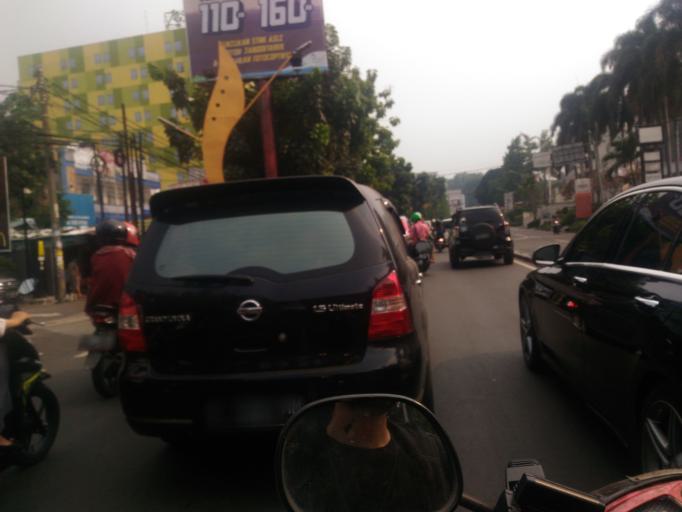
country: ID
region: West Java
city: Bogor
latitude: -6.5926
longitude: 106.8048
